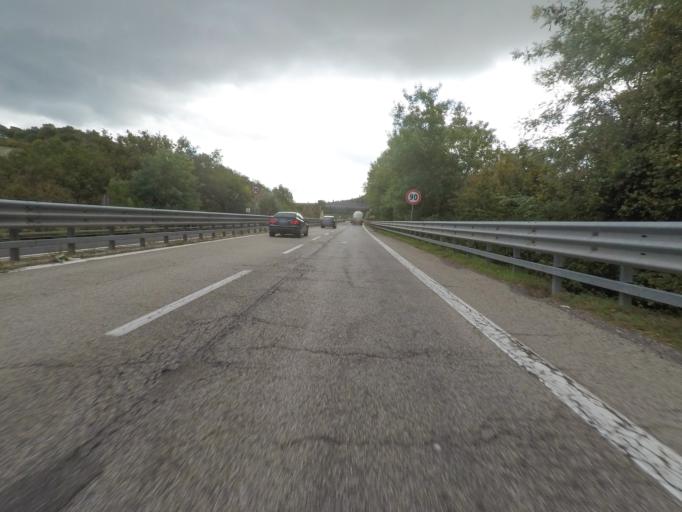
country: IT
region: Tuscany
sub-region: Provincia di Siena
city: Rapolano Terme
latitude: 43.3129
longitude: 11.5791
